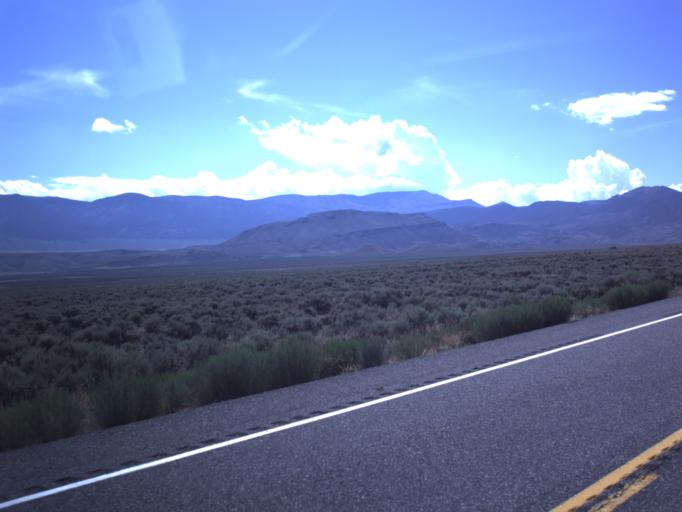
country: US
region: Utah
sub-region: Piute County
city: Junction
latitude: 38.3674
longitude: -112.2246
